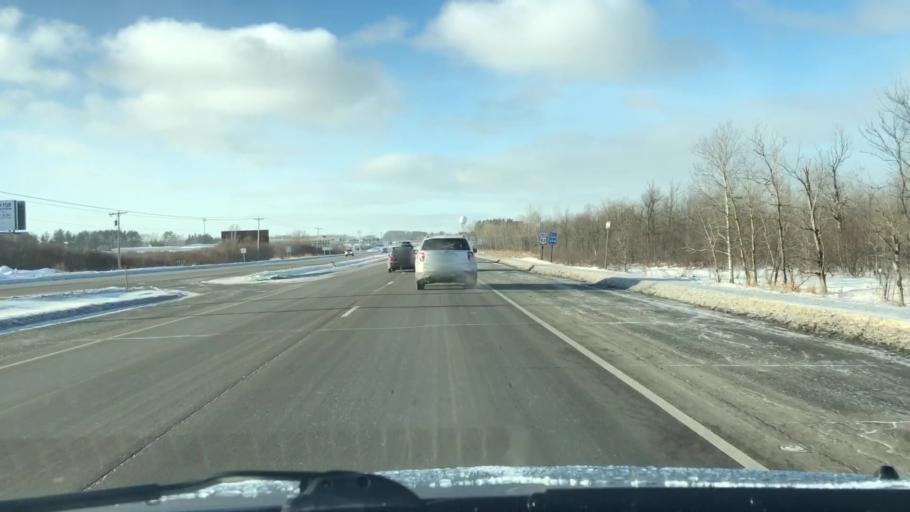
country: US
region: Minnesota
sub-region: Saint Louis County
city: Hermantown
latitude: 46.8289
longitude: -92.1975
